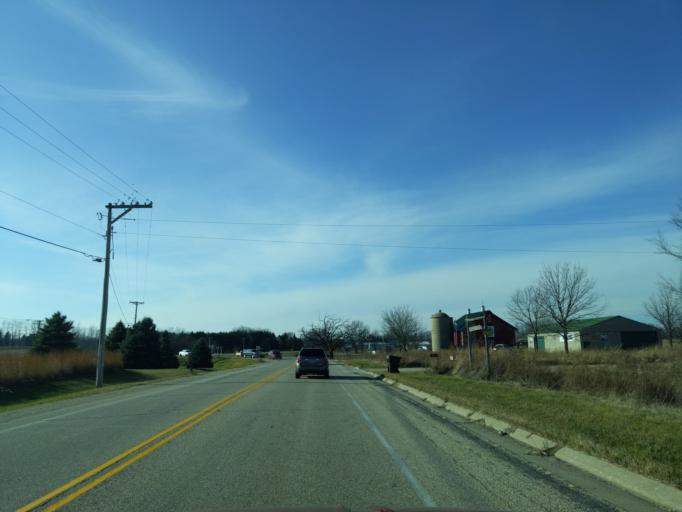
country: US
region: Wisconsin
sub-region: Rock County
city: Milton
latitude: 42.8249
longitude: -88.9799
